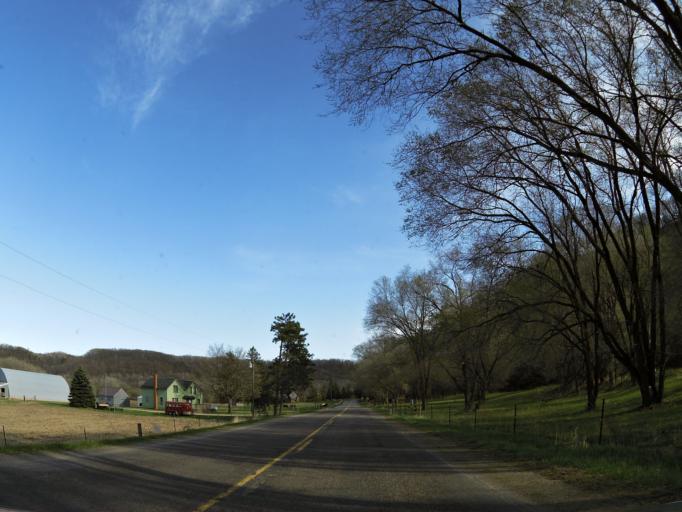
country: US
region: Minnesota
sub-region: Goodhue County
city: Red Wing
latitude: 44.6352
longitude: -92.5819
